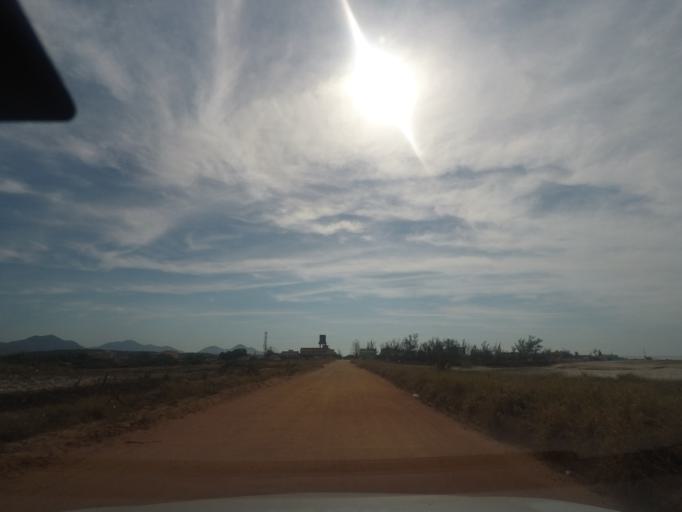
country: BR
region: Rio de Janeiro
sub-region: Marica
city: Marica
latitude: -22.9594
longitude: -42.8304
